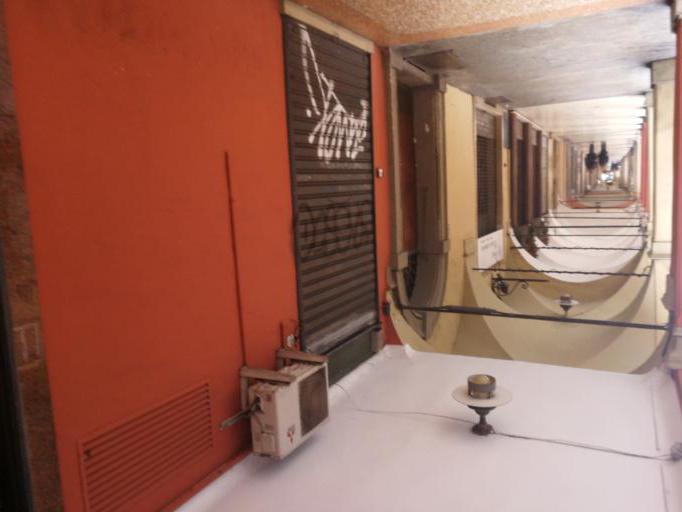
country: IT
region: Emilia-Romagna
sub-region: Provincia di Bologna
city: Bologna
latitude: 44.4973
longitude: 11.3329
